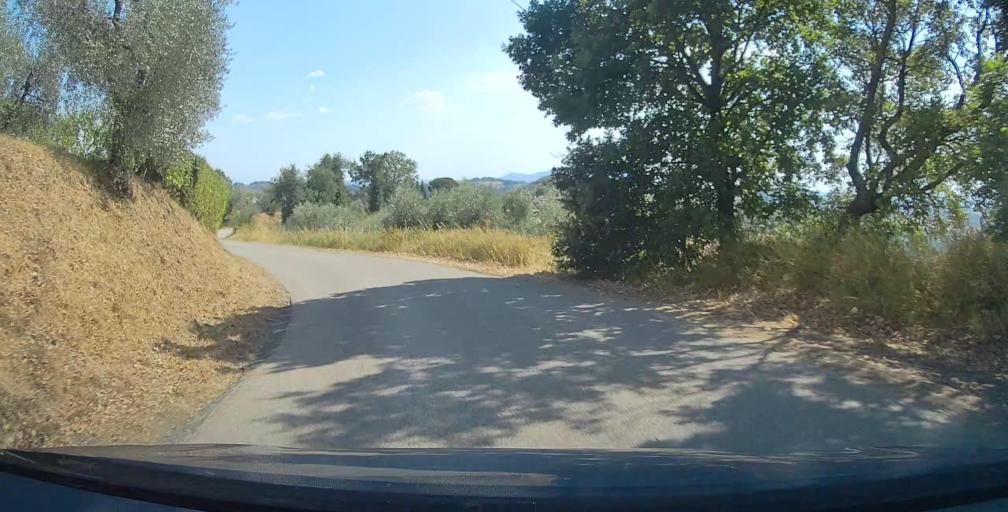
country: IT
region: Umbria
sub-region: Provincia di Terni
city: Calvi dell'Umbria
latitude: 42.3760
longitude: 12.5661
